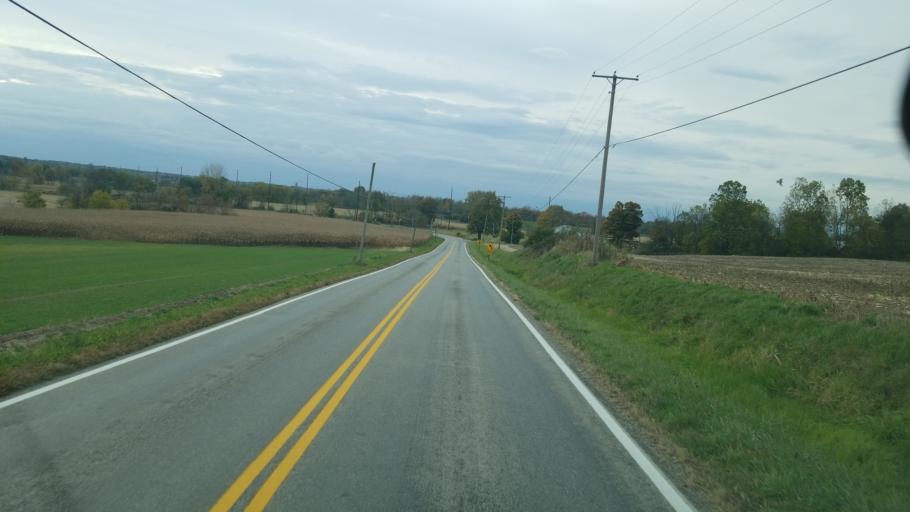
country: US
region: Ohio
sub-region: Ashland County
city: Ashland
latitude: 40.8772
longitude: -82.2626
